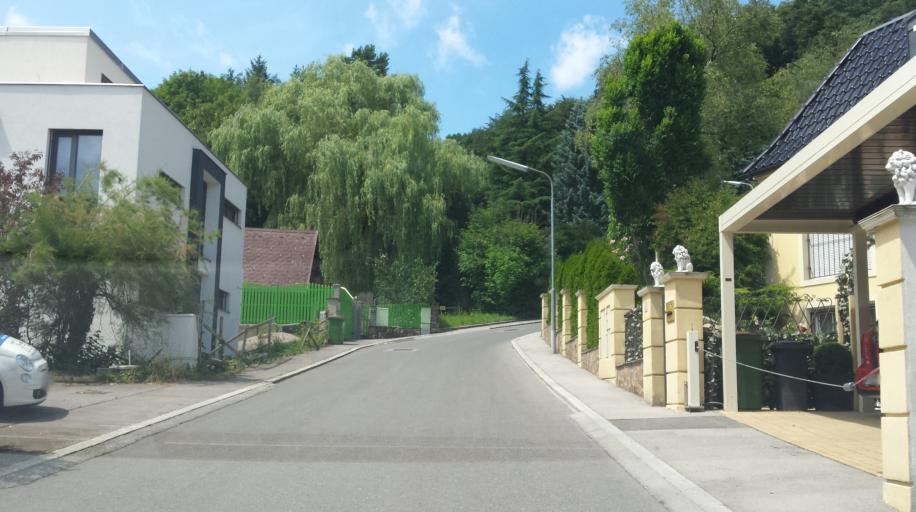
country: AT
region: Lower Austria
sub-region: Politischer Bezirk Wien-Umgebung
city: Mauerbach
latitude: 48.2469
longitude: 16.2161
